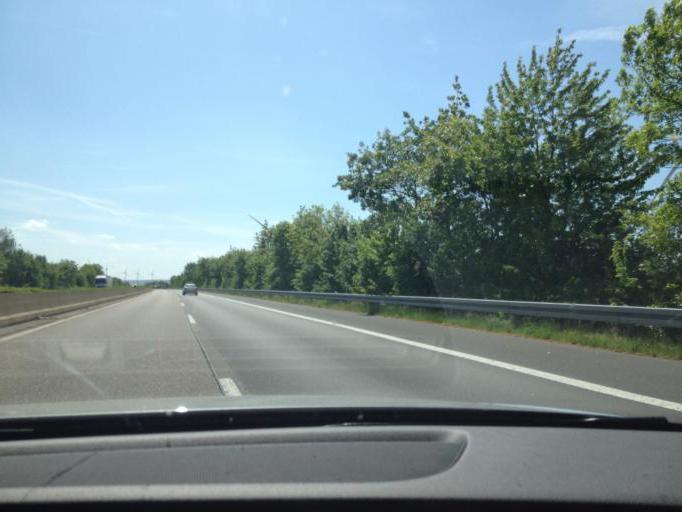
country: DE
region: North Rhine-Westphalia
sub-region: Regierungsbezirk Koln
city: Euskirchen
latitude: 50.7180
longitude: 6.7787
